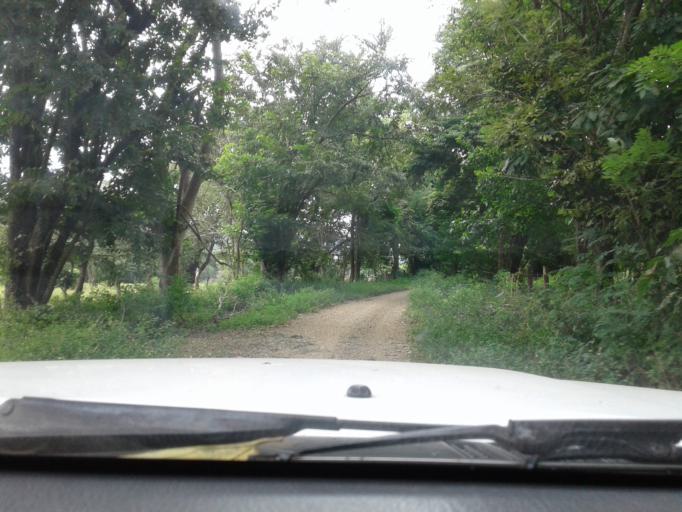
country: NI
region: Rivas
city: San Juan del Sur
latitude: 11.2296
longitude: -85.7836
